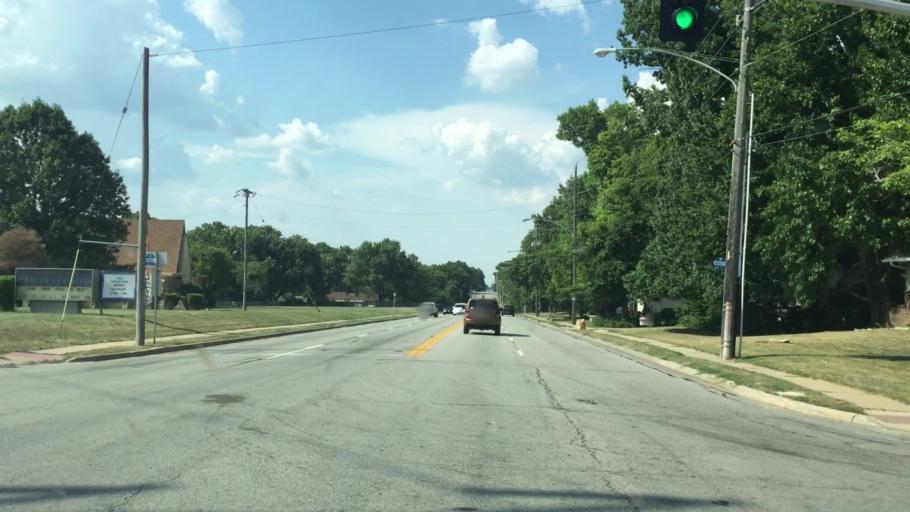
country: US
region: Kansas
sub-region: Johnson County
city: Merriam
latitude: 38.9951
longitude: -94.7145
